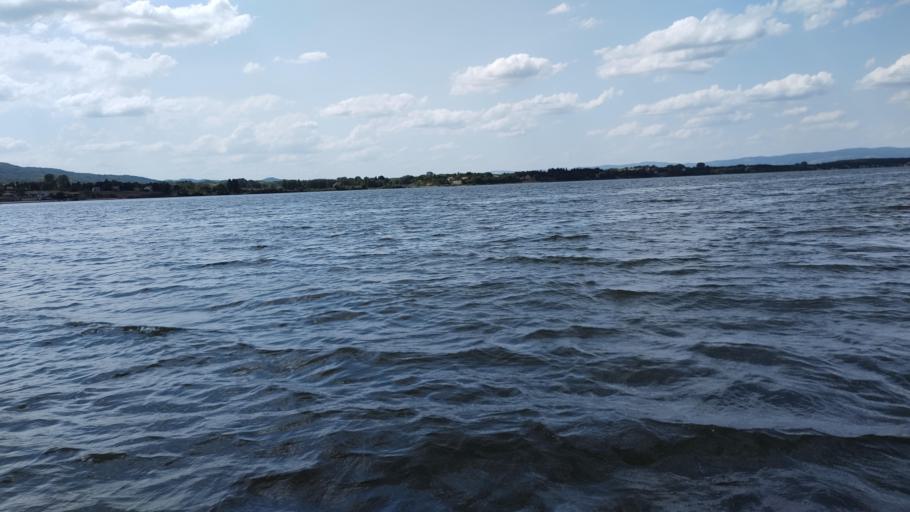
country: RS
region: Central Serbia
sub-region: Branicevski Okrug
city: Golubac
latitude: 44.6793
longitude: 21.6170
